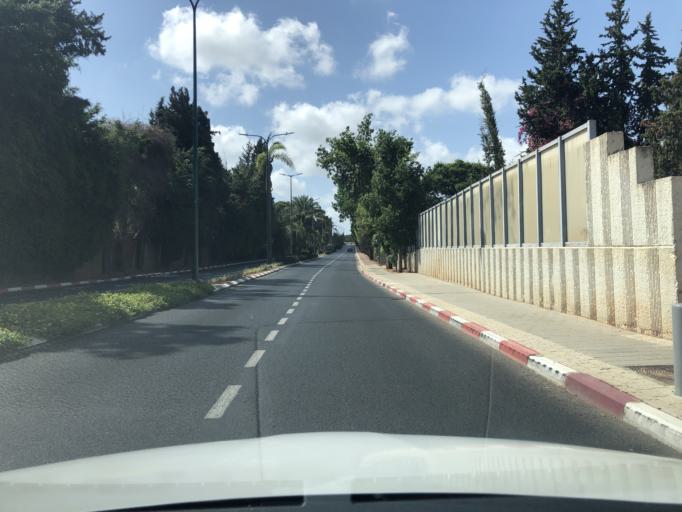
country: IL
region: Tel Aviv
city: Giv`at Shemu'el
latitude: 32.0589
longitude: 34.8493
